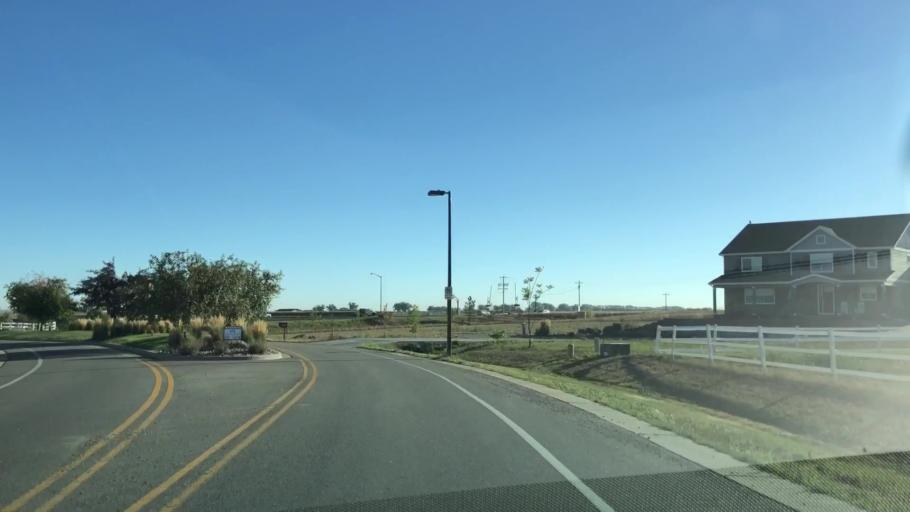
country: US
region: Colorado
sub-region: Larimer County
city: Loveland
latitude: 40.4644
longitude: -105.0354
